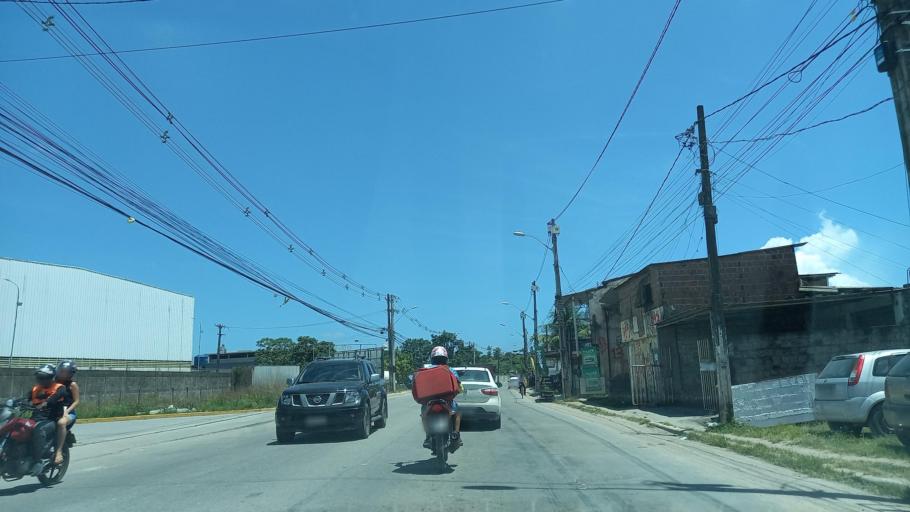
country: BR
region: Pernambuco
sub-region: Jaboatao Dos Guararapes
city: Jaboatao
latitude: -8.1542
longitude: -34.9594
